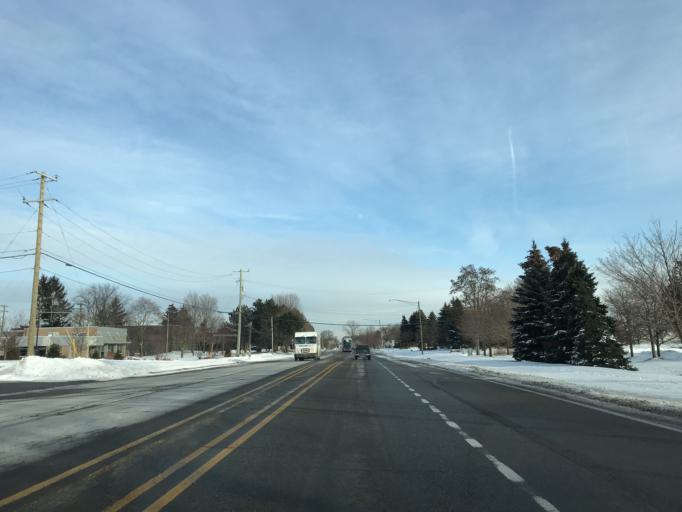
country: US
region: Michigan
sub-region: Oakland County
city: Wixom
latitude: 42.5240
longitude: -83.5491
